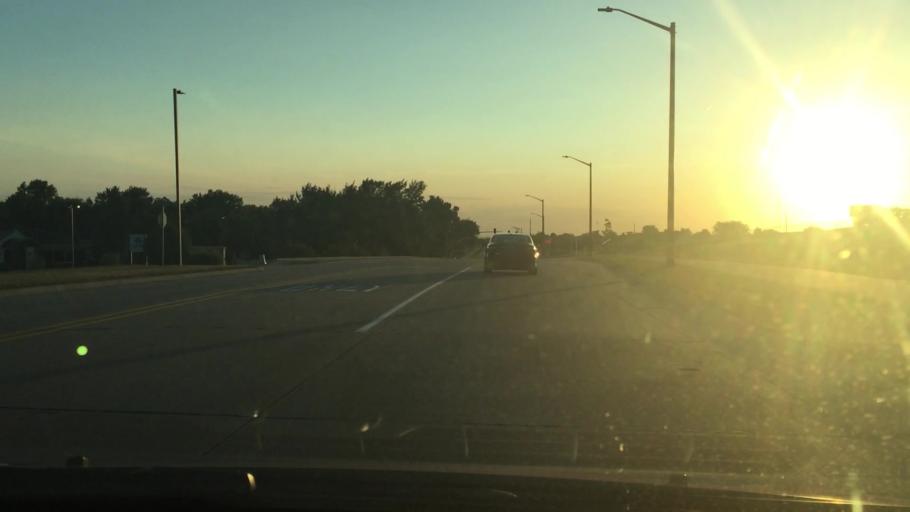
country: US
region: Iowa
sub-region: Muscatine County
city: Muscatine
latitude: 41.4360
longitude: -91.0724
